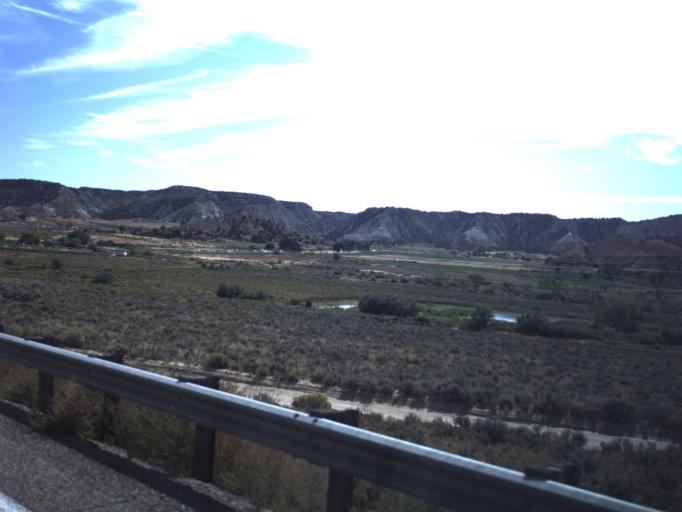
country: US
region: Utah
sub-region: Garfield County
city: Panguitch
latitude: 37.5588
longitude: -112.0192
